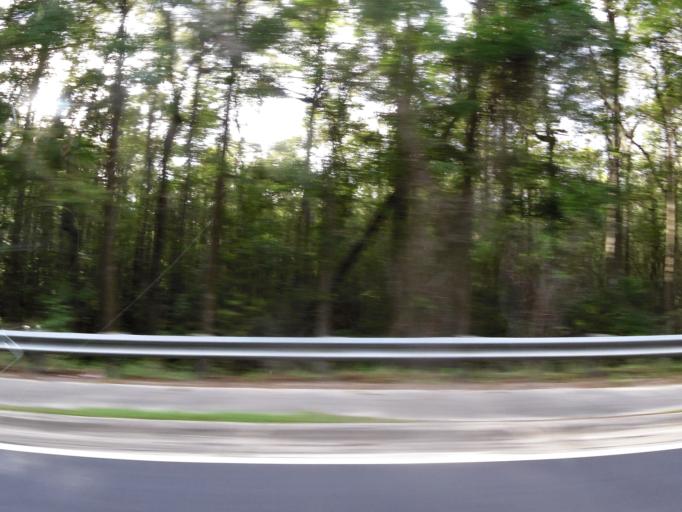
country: US
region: Georgia
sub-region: Liberty County
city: Midway
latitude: 31.8018
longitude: -81.4323
